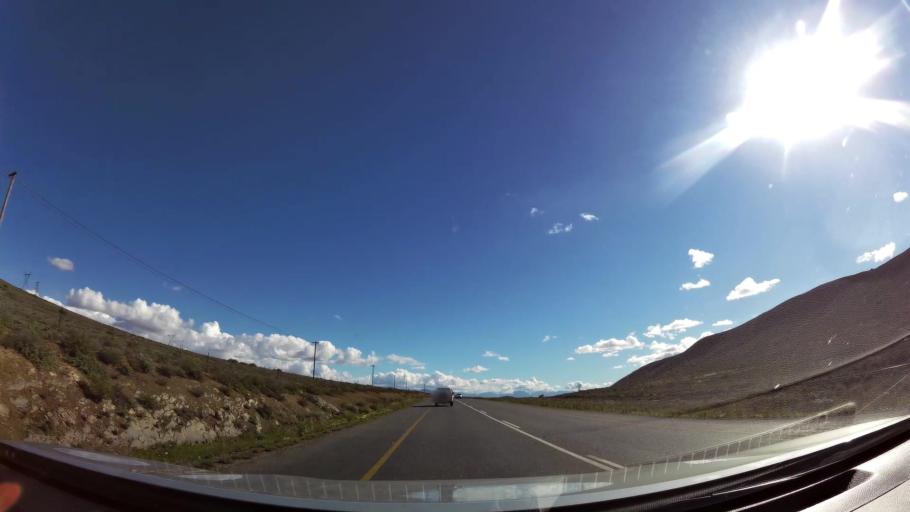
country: ZA
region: Western Cape
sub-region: Cape Winelands District Municipality
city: Worcester
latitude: -33.7350
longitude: 19.6590
